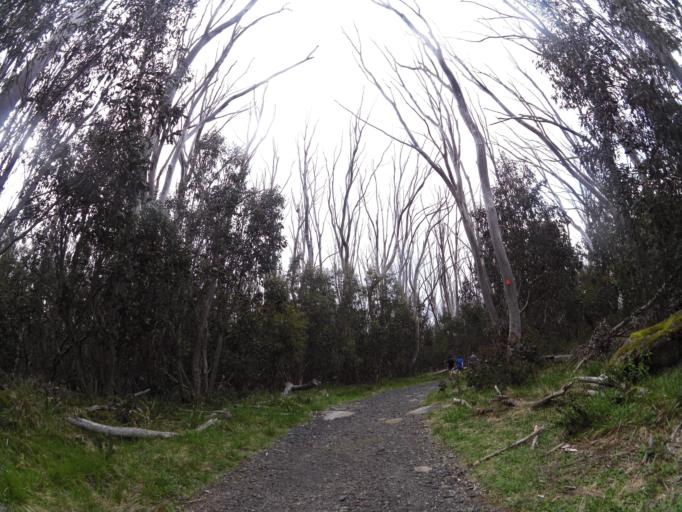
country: AU
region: Victoria
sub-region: Yarra Ranges
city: Millgrove
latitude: -37.5009
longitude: 145.8788
